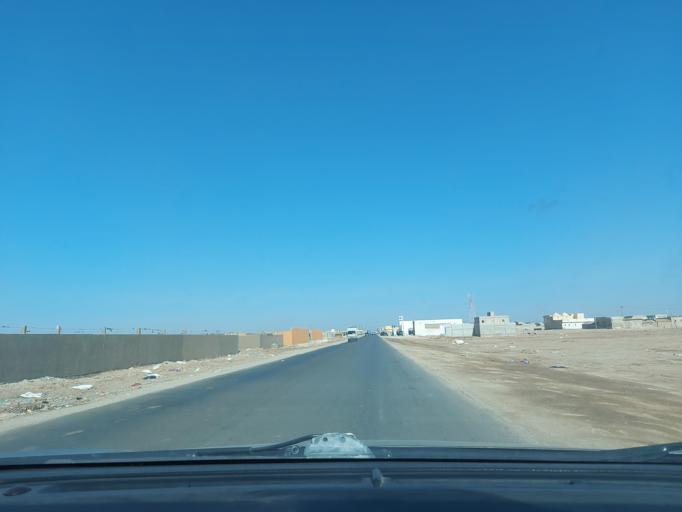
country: MR
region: Nouakchott
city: Nouakchott
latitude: 18.0112
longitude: -15.9838
